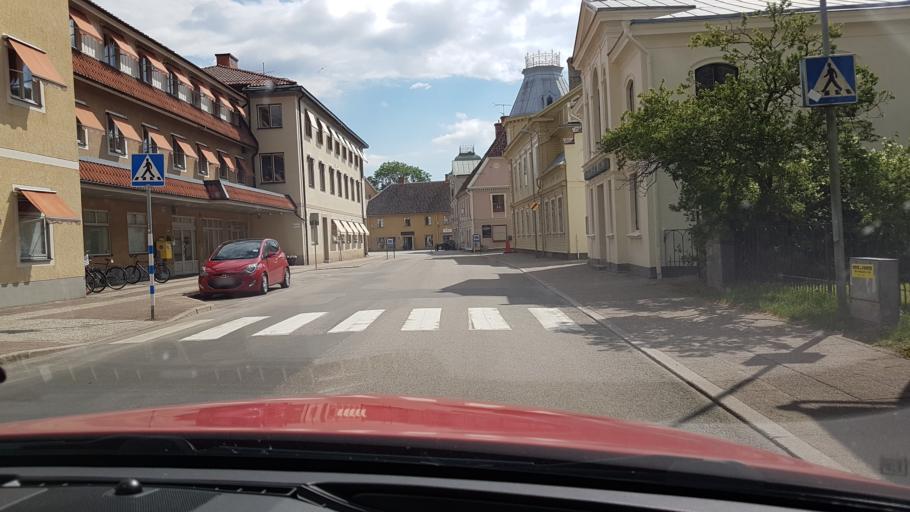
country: SE
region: Vaestra Goetaland
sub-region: Hjo Kommun
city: Hjo
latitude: 58.3011
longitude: 14.2862
